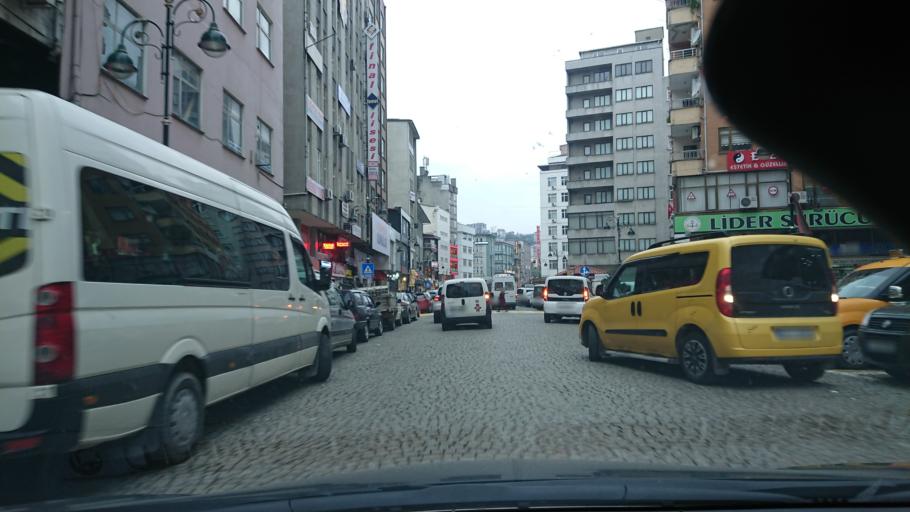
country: TR
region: Rize
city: Rize
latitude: 41.0246
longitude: 40.5218
